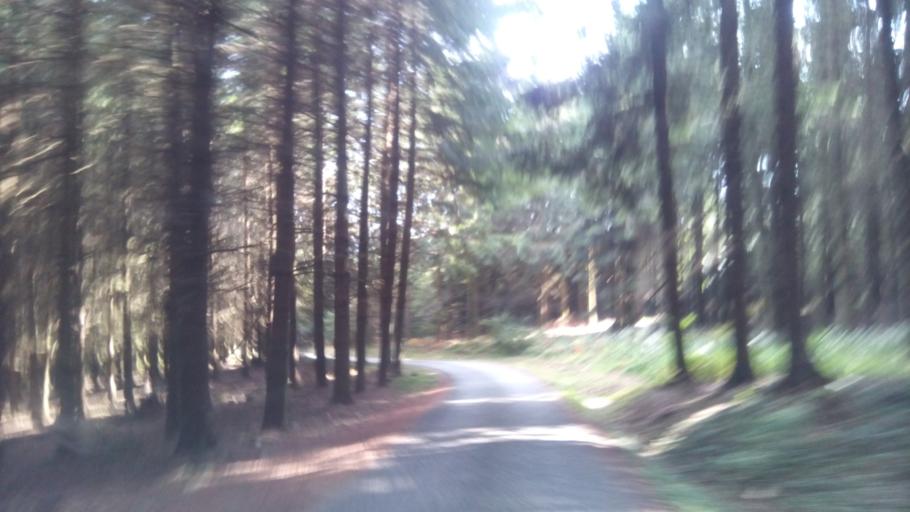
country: FR
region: Rhone-Alpes
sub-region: Departement du Rhone
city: Beaujeu
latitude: 46.2062
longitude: 4.5328
